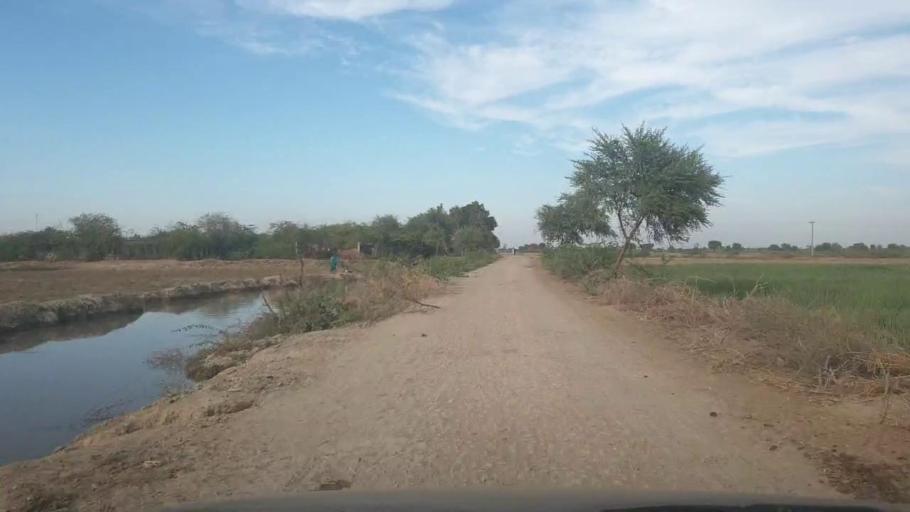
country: PK
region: Sindh
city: Samaro
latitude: 25.3288
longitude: 69.2547
